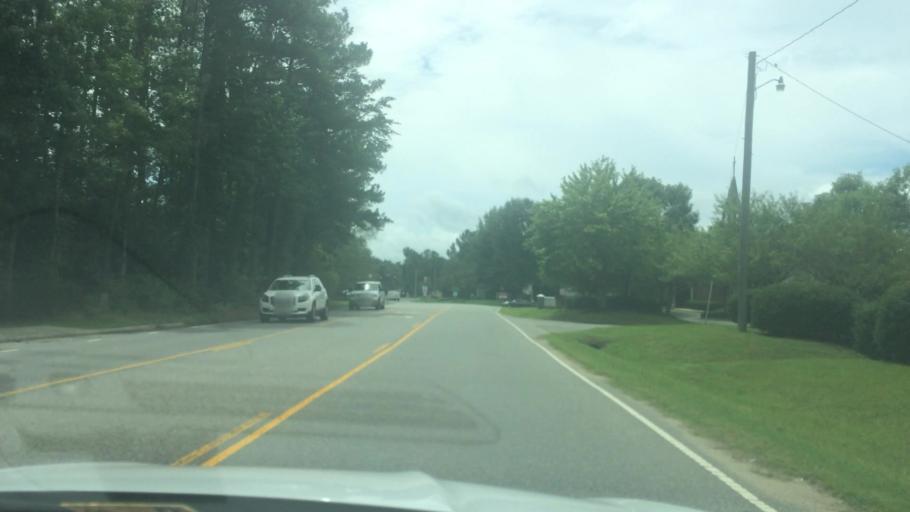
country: US
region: Virginia
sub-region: James City County
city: Williamsburg
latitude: 37.2542
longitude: -76.7658
